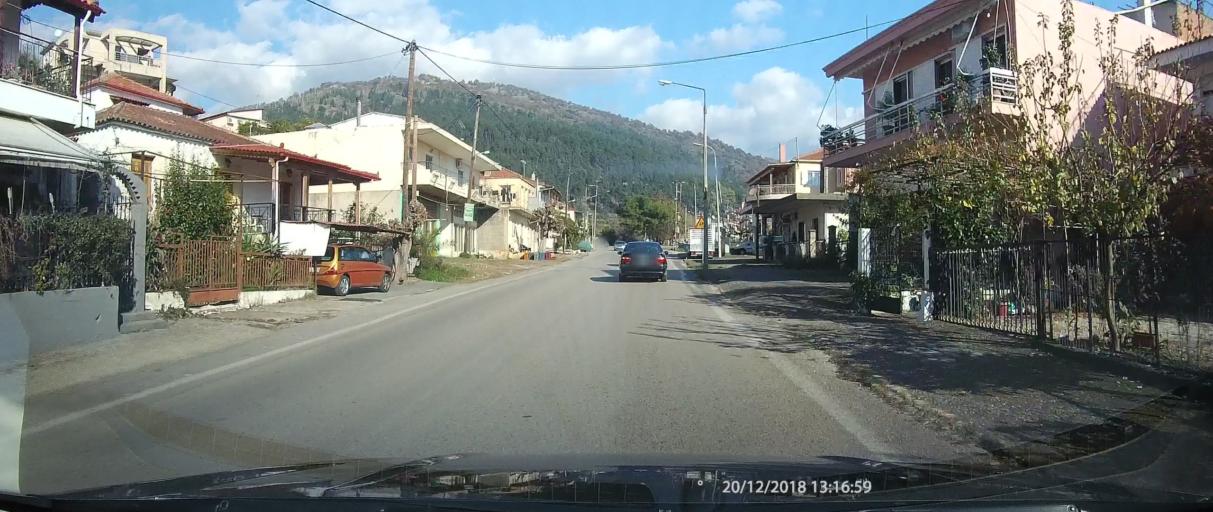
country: GR
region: West Greece
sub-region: Nomos Aitolias kai Akarnanias
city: Paravola
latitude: 38.6119
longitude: 21.5158
